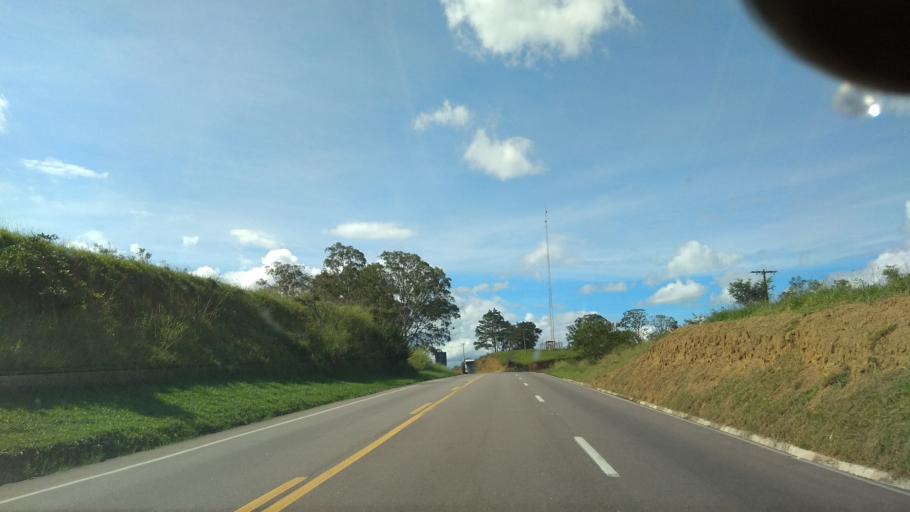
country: BR
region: Bahia
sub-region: Santa Ines
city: Santa Ines
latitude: -13.2013
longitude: -40.0128
